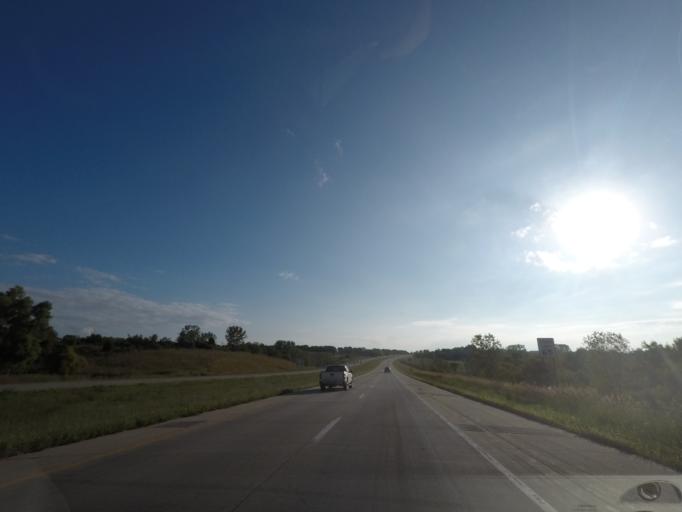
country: US
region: Iowa
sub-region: Warren County
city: Carlisle
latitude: 41.5098
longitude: -93.5571
